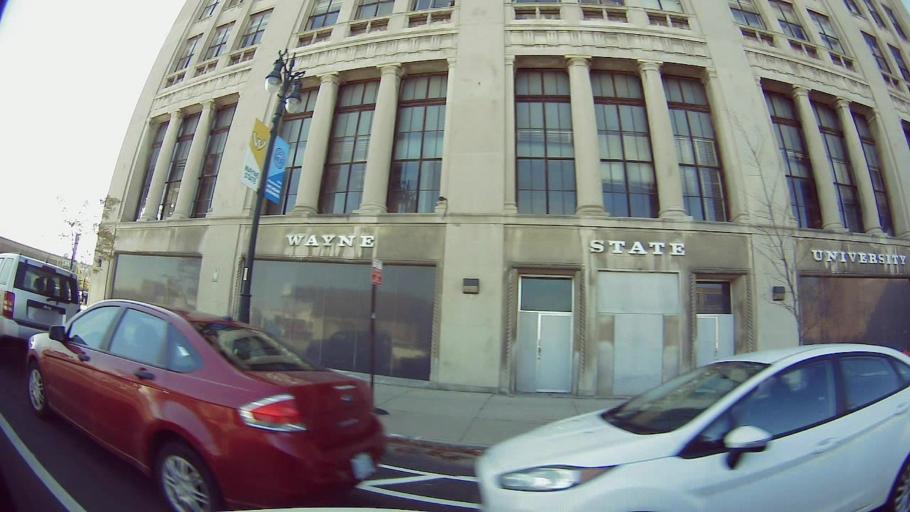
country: US
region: Michigan
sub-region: Wayne County
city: Hamtramck
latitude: 42.3644
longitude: -83.0715
